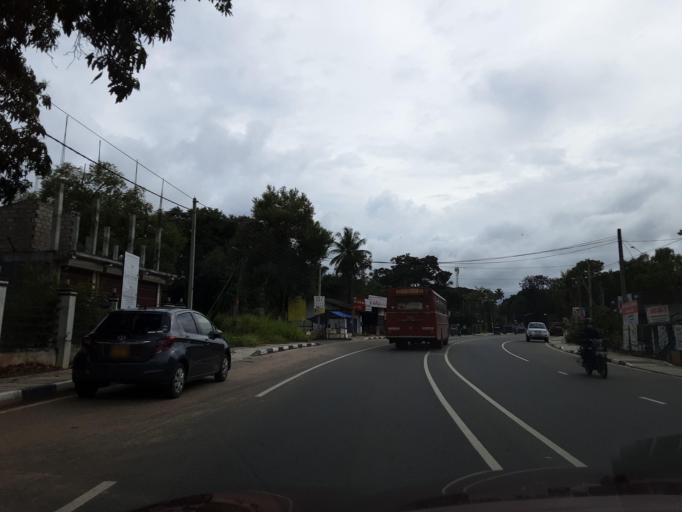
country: LK
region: Eastern Province
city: Ampara
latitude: 7.4005
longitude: 81.2432
